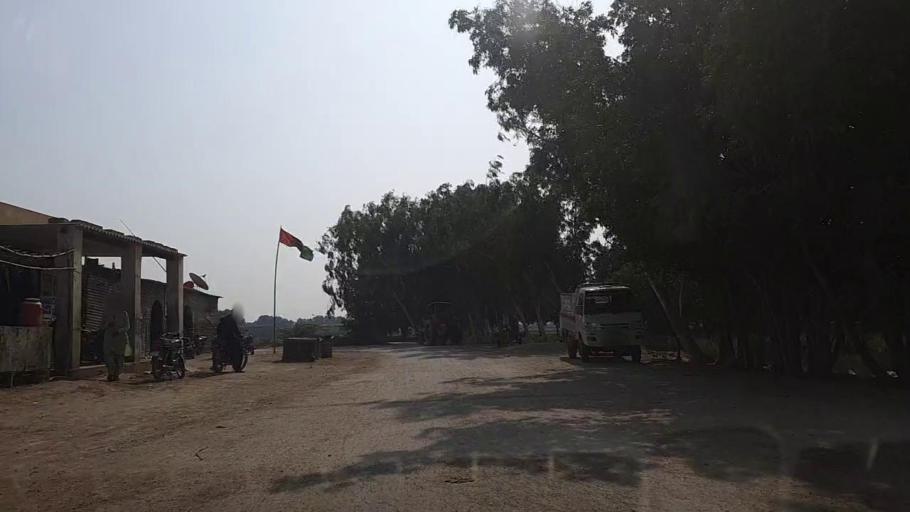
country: PK
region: Sindh
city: Keti Bandar
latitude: 24.2238
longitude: 67.6665
